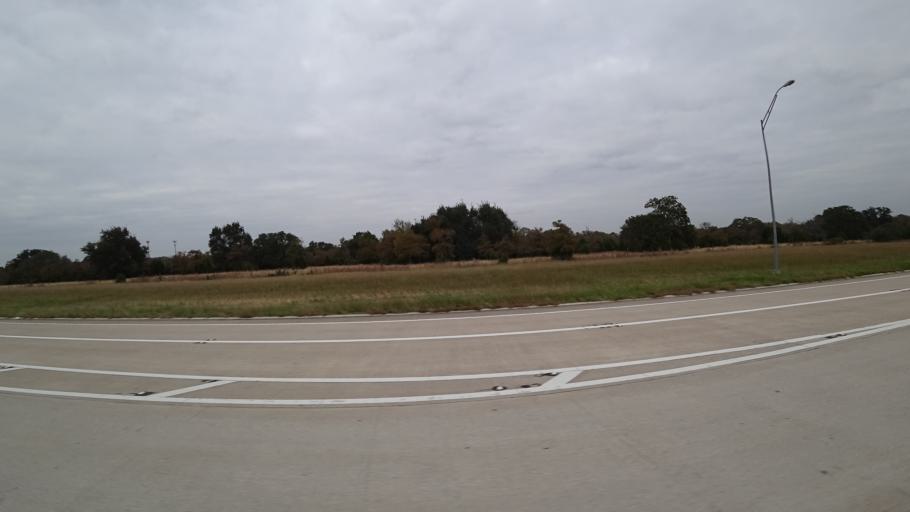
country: US
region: Texas
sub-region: Williamson County
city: Brushy Creek
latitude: 30.4783
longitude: -97.7312
